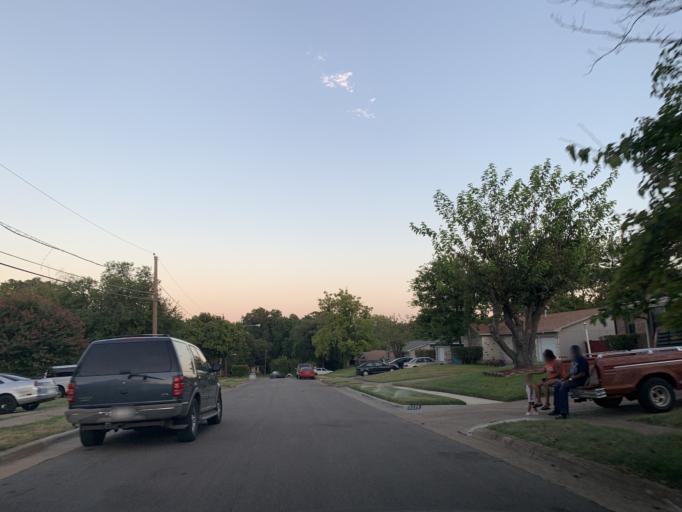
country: US
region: Texas
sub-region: Dallas County
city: Hutchins
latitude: 32.6709
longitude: -96.8007
